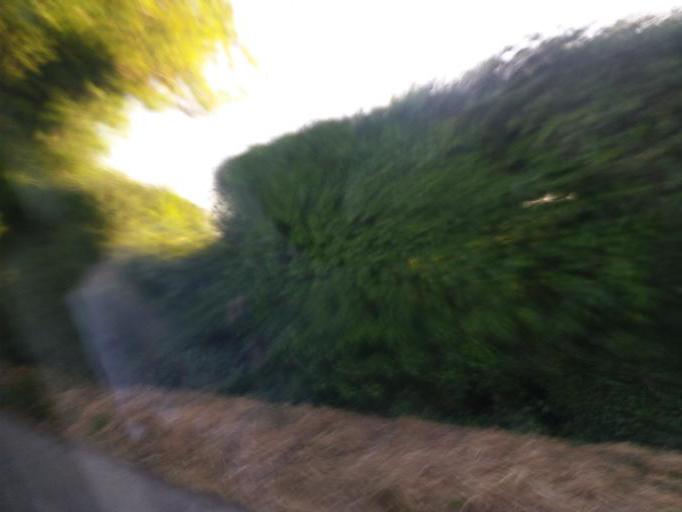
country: IE
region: Leinster
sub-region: An Mhi
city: Ashbourne
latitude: 53.5590
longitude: -6.3568
